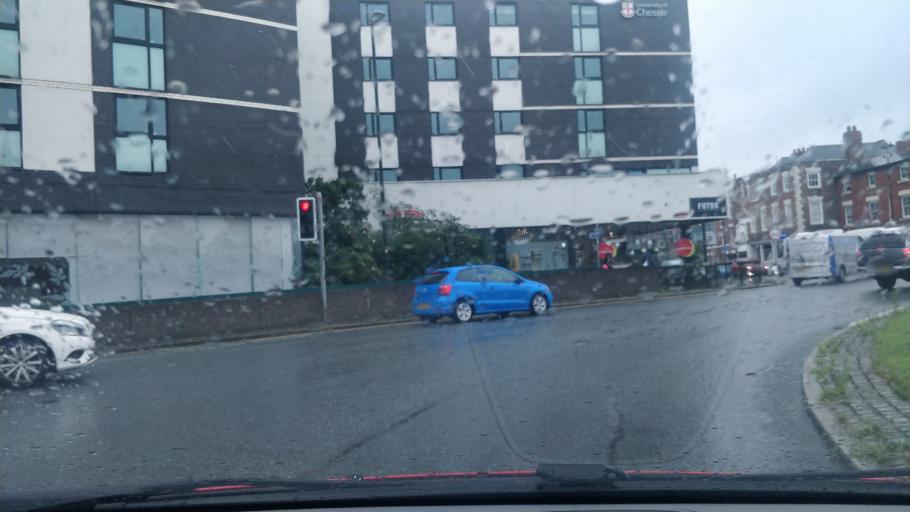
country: GB
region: England
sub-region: Cheshire West and Chester
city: Chester
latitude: 53.1954
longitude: -2.8935
